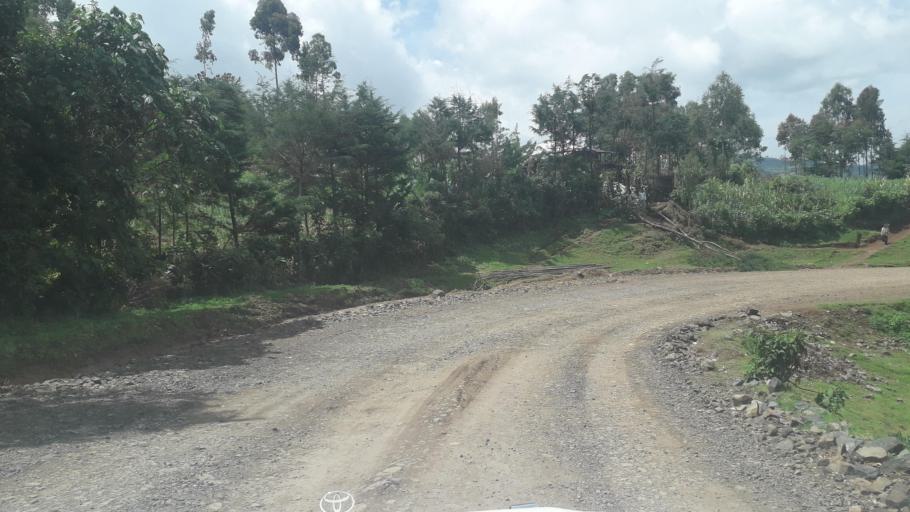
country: ET
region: Oromiya
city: Jima
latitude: 7.4538
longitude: 36.8713
